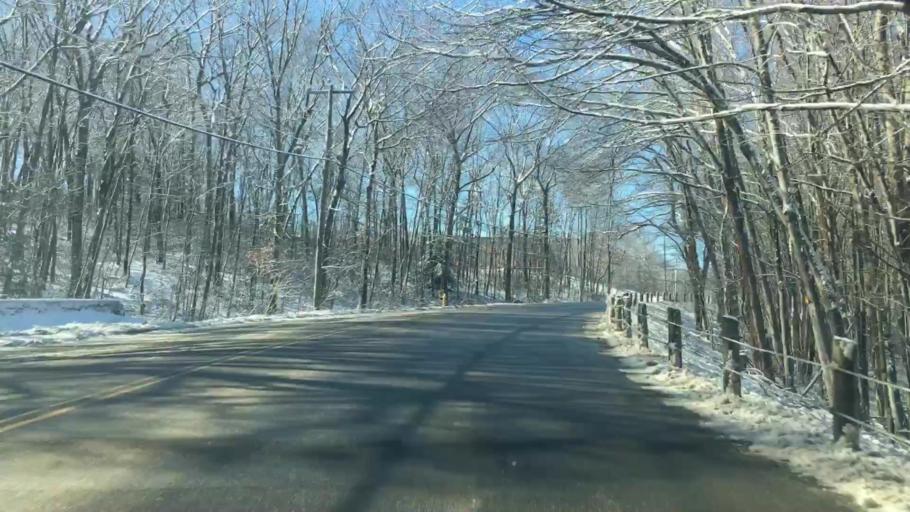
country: US
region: Connecticut
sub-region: Litchfield County
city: Oakville
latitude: 41.6097
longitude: -73.0687
